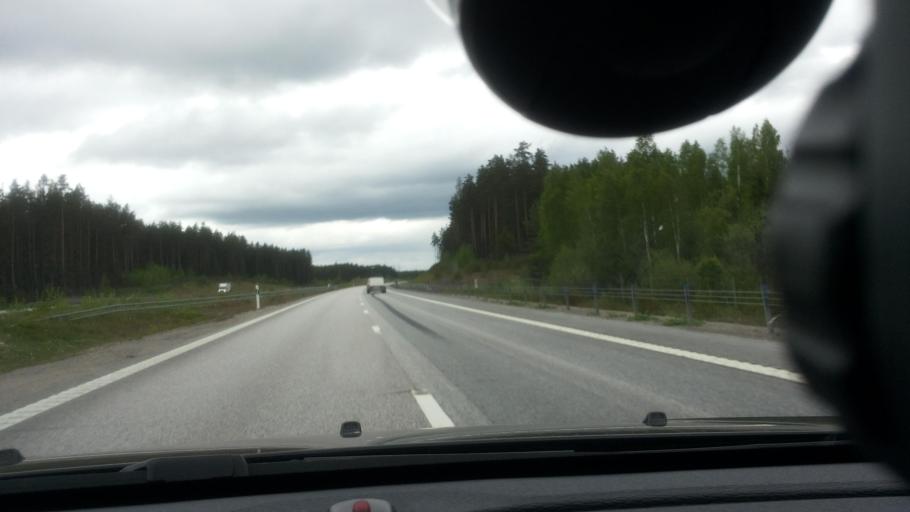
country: SE
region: Uppsala
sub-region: Tierps Kommun
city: Tierp
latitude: 60.2775
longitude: 17.5020
